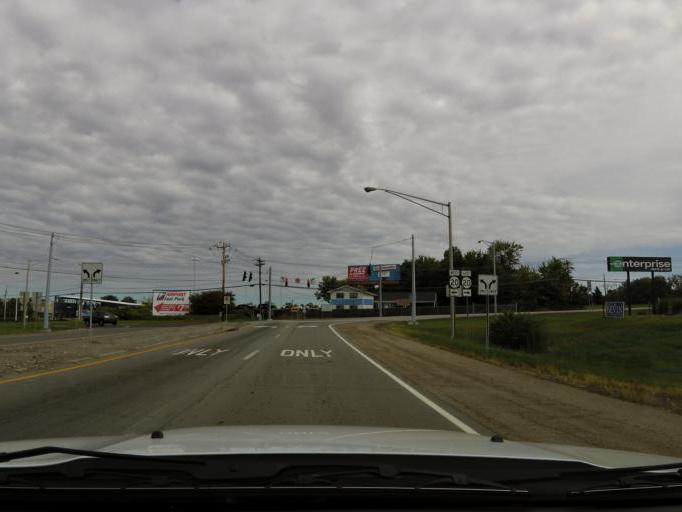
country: US
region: Ohio
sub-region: Hamilton County
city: Delhi Hills
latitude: 39.0732
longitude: -84.6536
